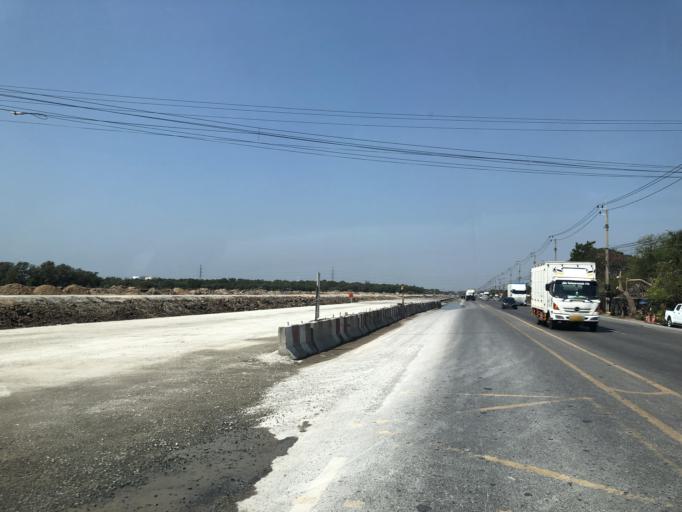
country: TH
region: Samut Prakan
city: Bang Bo
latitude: 13.4956
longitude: 100.8523
